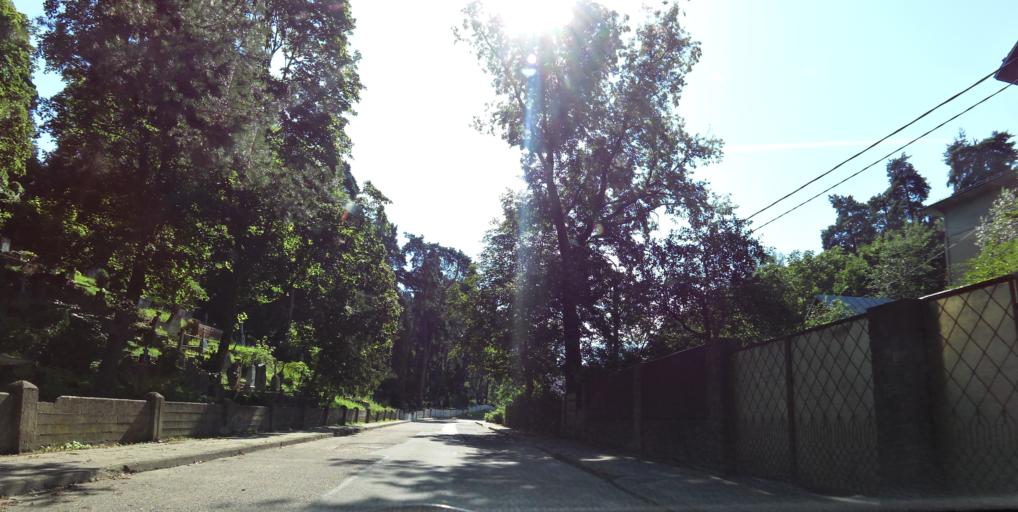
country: LT
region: Vilnius County
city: Rasos
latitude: 54.6947
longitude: 25.3105
